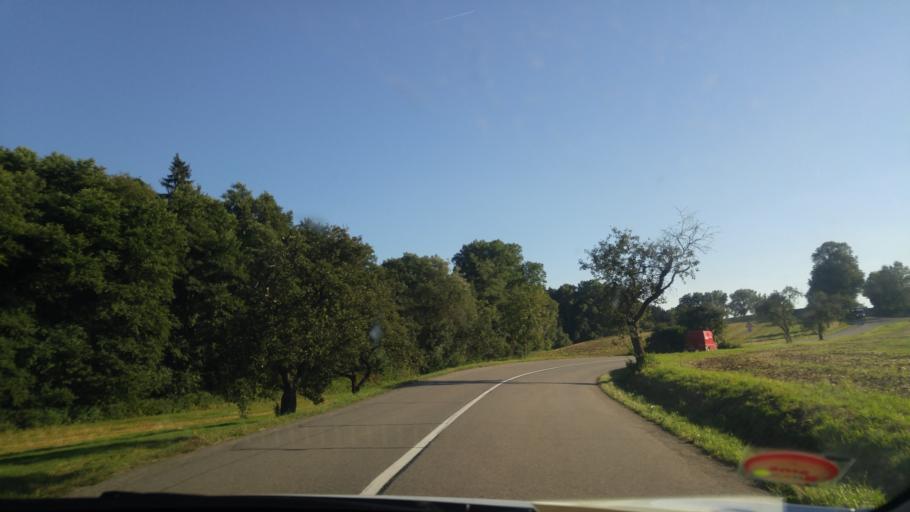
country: CZ
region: South Moravian
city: Veverska Bityska
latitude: 49.2432
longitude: 16.4455
